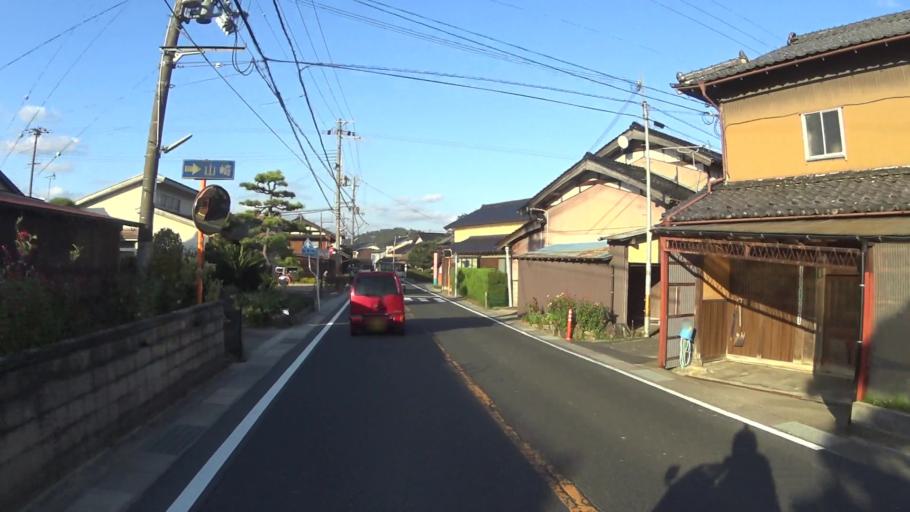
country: JP
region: Kyoto
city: Miyazu
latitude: 35.5908
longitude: 135.0396
